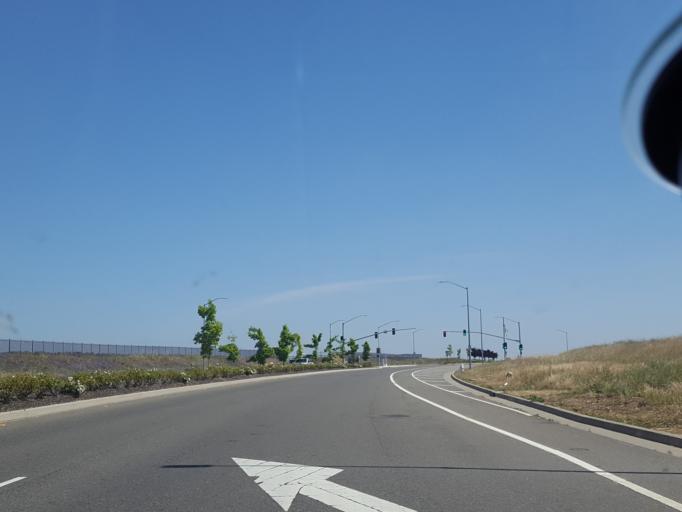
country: US
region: California
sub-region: Sacramento County
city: Rancho Cordova
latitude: 38.5702
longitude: -121.2677
